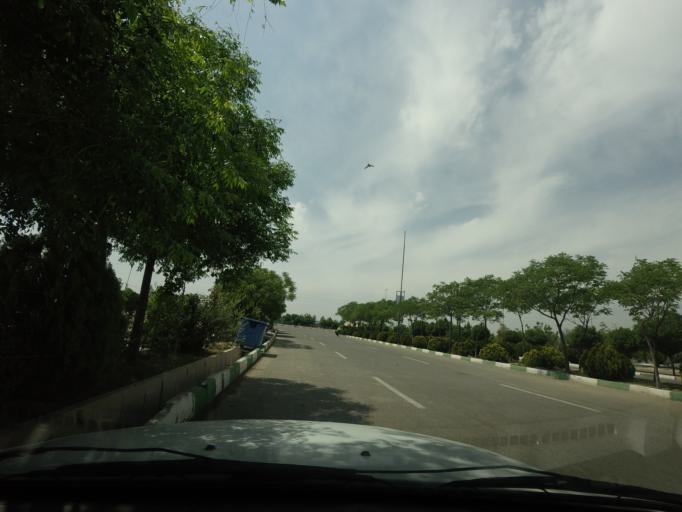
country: IR
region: Tehran
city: Shahrak-e Emam Hasan-e Mojtaba
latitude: 35.5176
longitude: 51.3803
